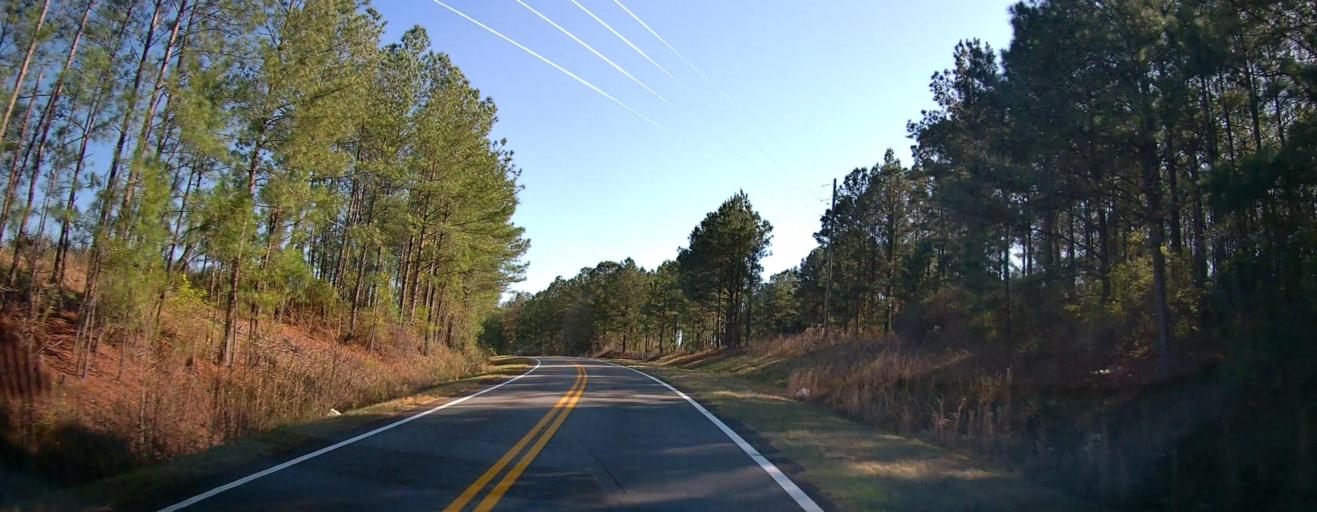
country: US
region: Georgia
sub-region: Taylor County
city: Reynolds
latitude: 32.5579
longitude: -84.0013
